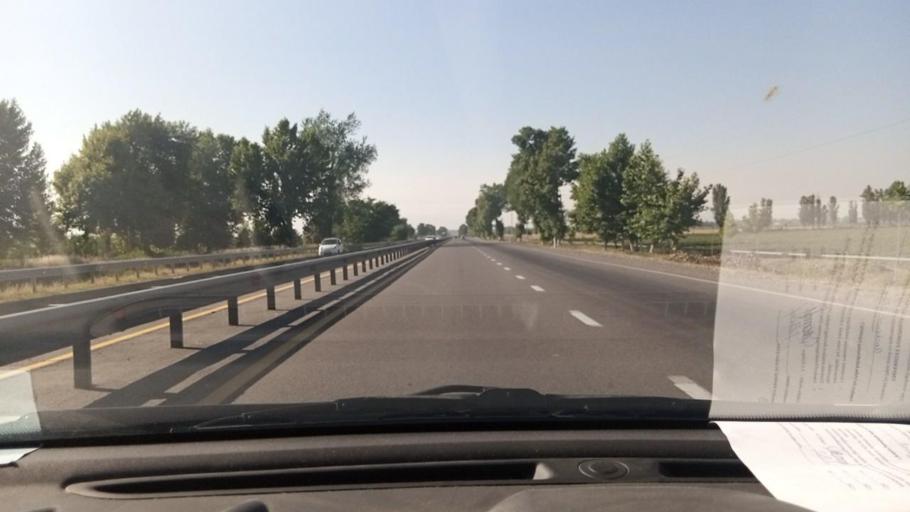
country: UZ
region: Toshkent Shahri
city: Bektemir
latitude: 41.1696
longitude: 69.4146
